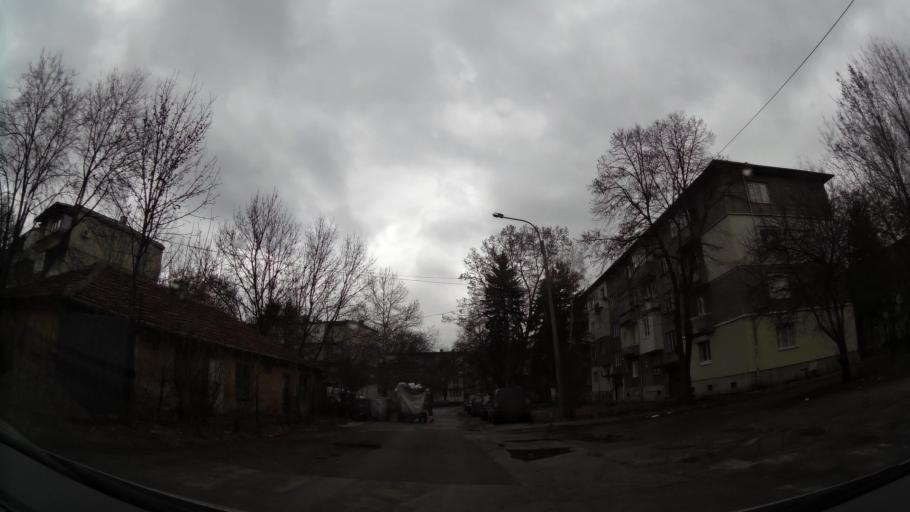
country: BG
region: Sofia-Capital
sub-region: Stolichna Obshtina
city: Sofia
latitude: 42.7356
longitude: 23.3007
